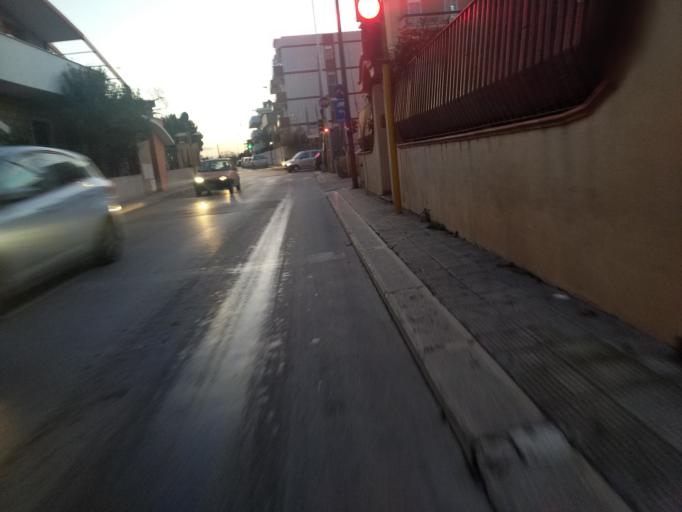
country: IT
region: Apulia
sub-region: Provincia di Bari
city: Modugno
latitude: 41.0766
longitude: 16.7848
